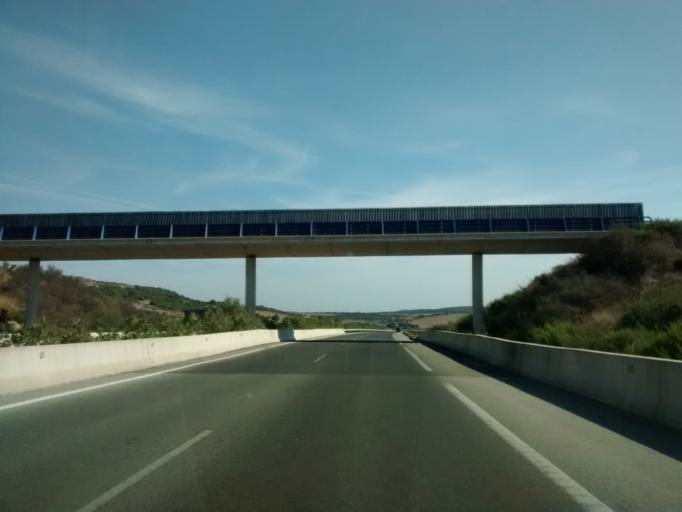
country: ES
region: Andalusia
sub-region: Provincia de Cadiz
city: Conil de la Frontera
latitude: 36.3276
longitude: -6.0544
